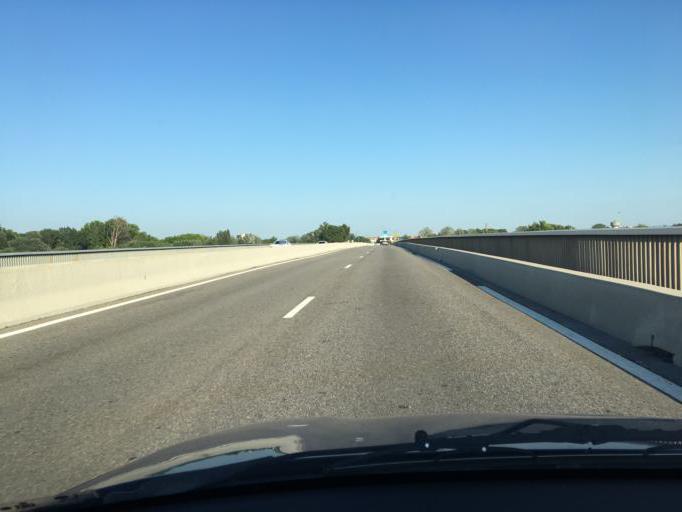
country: FR
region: Provence-Alpes-Cote d'Azur
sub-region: Departement du Vaucluse
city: Avignon
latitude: 43.9478
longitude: 4.7880
